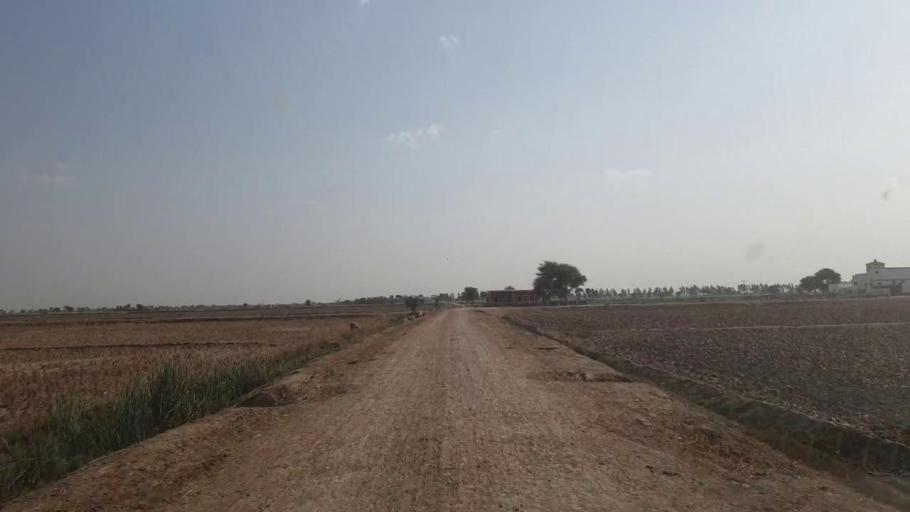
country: PK
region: Sindh
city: Kario
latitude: 24.5545
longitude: 68.5084
